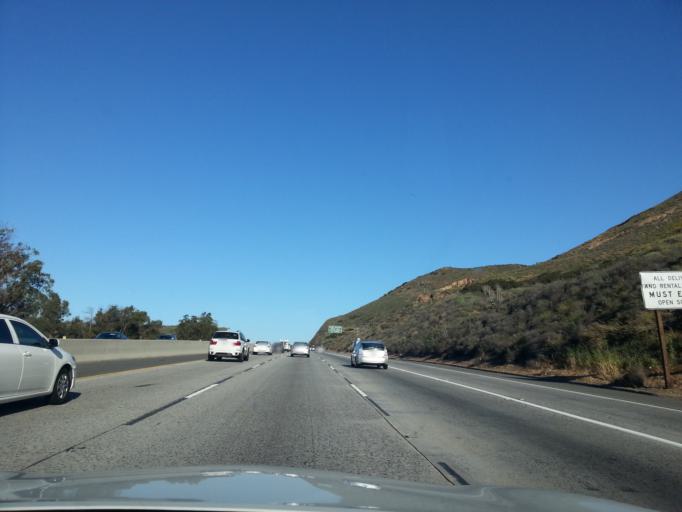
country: US
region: California
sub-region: Ventura County
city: Casa Conejo
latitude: 34.1952
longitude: -118.9498
